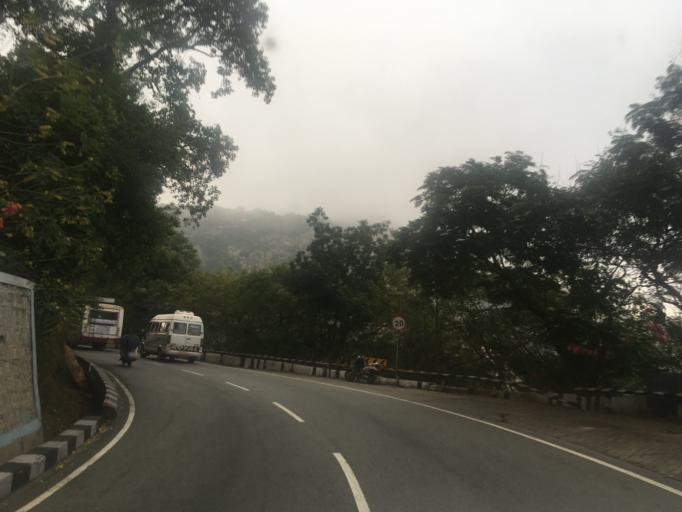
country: IN
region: Andhra Pradesh
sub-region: Chittoor
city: Tirumala
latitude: 13.6658
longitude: 79.3495
